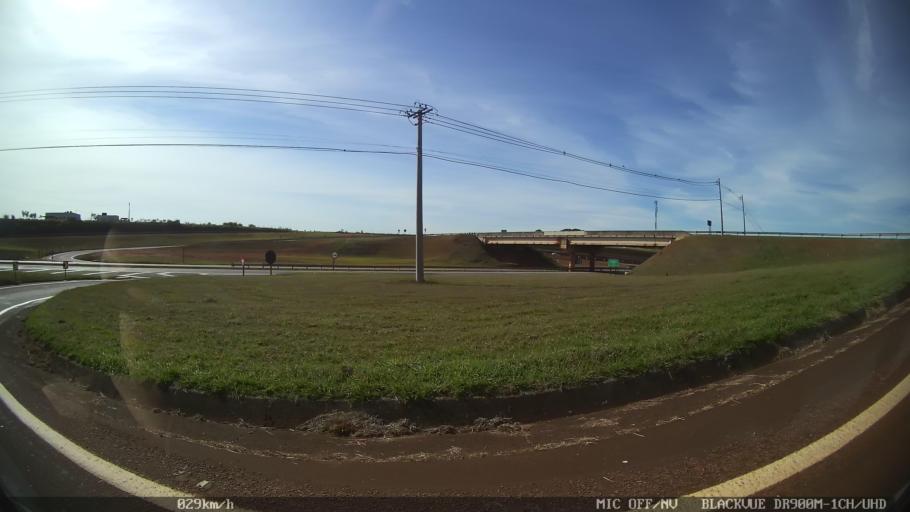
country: BR
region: Sao Paulo
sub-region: Rio Das Pedras
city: Rio das Pedras
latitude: -22.7825
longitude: -47.5881
